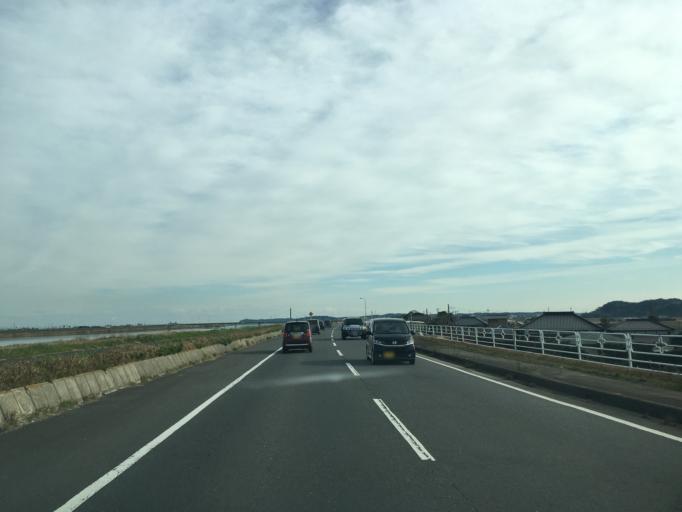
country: JP
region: Chiba
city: Katori-shi
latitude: 35.9143
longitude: 140.4690
